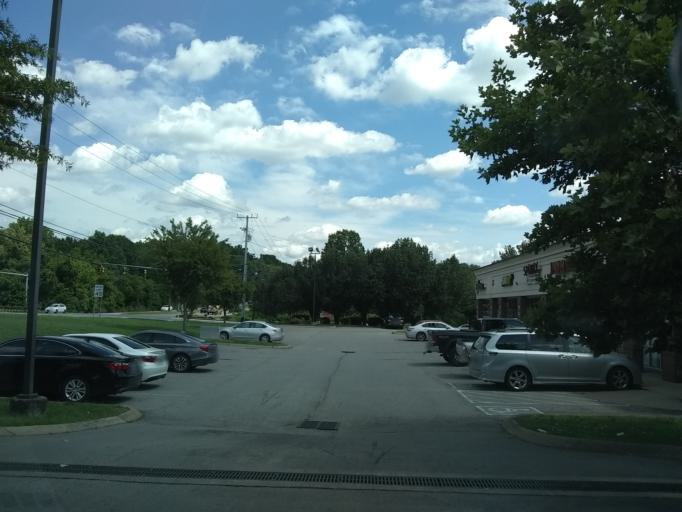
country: US
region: Tennessee
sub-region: Davidson County
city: Nashville
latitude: 36.1365
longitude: -86.6997
